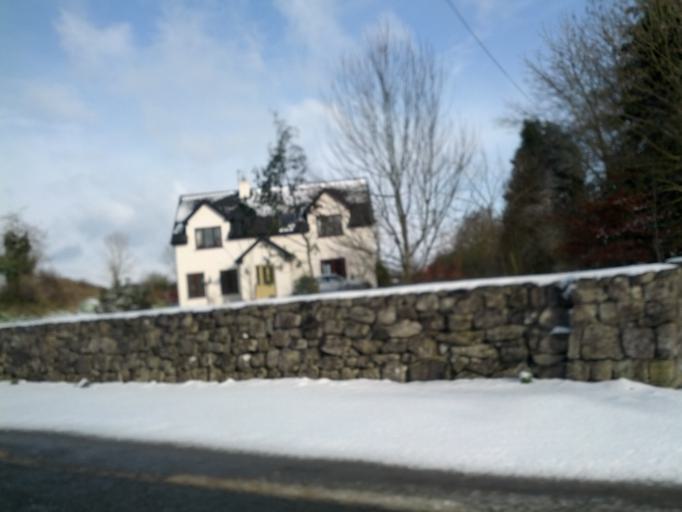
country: IE
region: Connaught
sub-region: County Galway
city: Athenry
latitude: 53.2074
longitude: -8.7583
